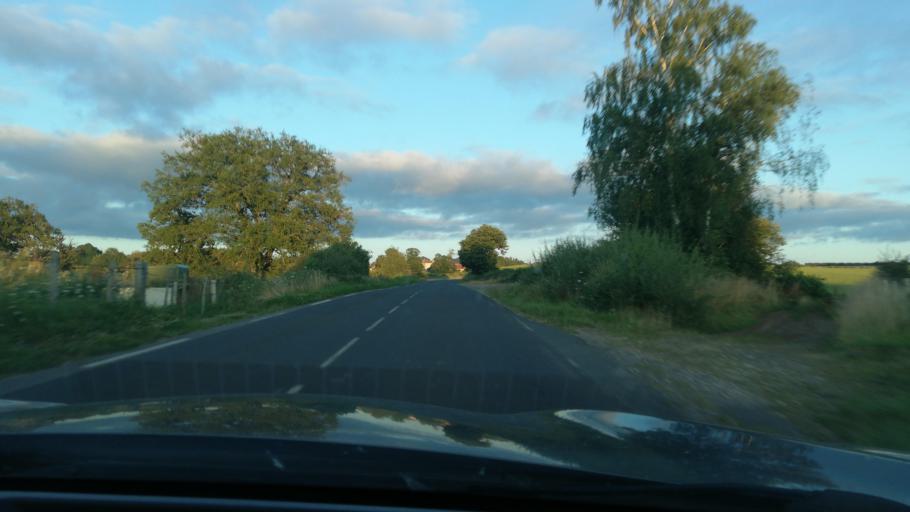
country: FR
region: Auvergne
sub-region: Departement du Cantal
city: Laroquebrou
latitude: 44.9598
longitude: 2.1425
